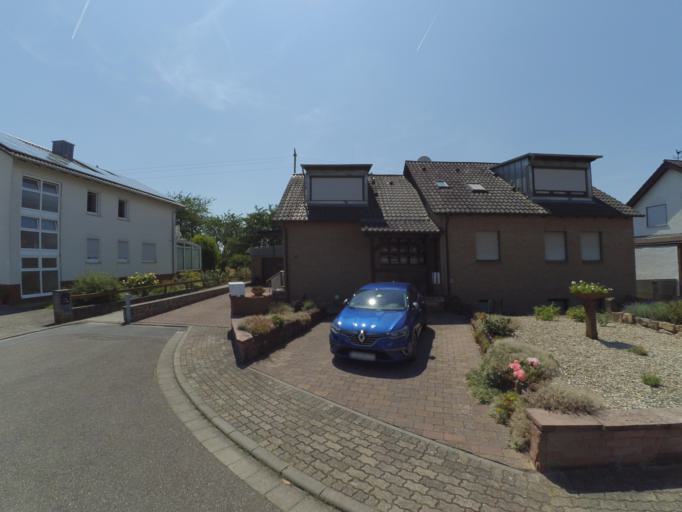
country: DE
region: Rheinland-Pfalz
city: Bornheim
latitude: 49.2193
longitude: 8.1564
